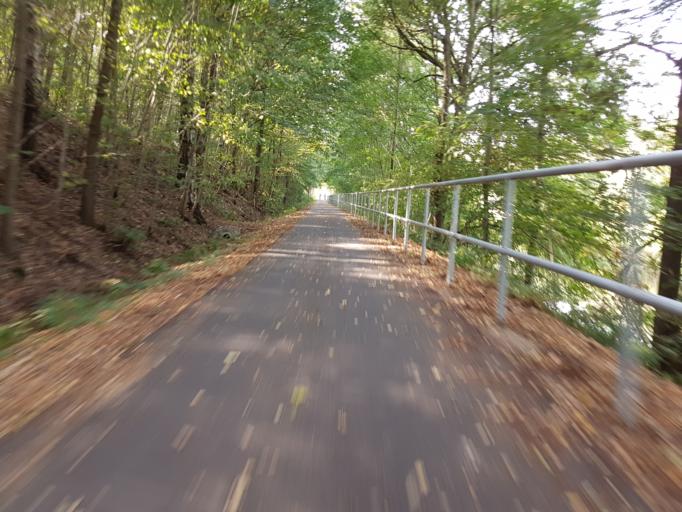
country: DE
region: Saxony
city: Claussnitz
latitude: 50.9157
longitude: 12.8827
